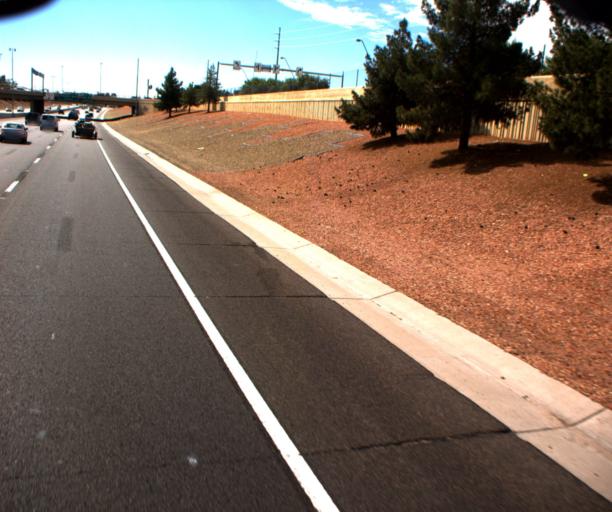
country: US
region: Arizona
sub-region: Maricopa County
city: San Carlos
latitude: 33.3369
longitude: -111.8932
